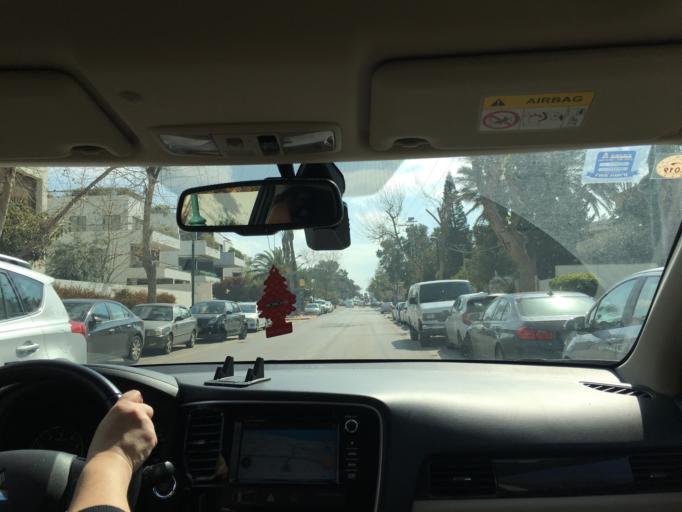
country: IL
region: Tel Aviv
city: Herzliya Pituah
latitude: 32.1805
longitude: 34.8066
